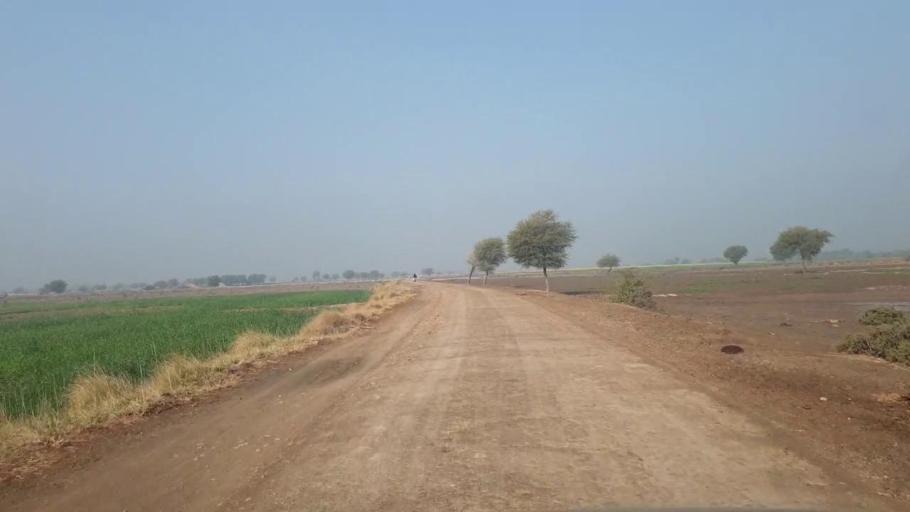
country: PK
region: Sindh
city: Shahdadpur
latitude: 25.9479
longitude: 68.5804
